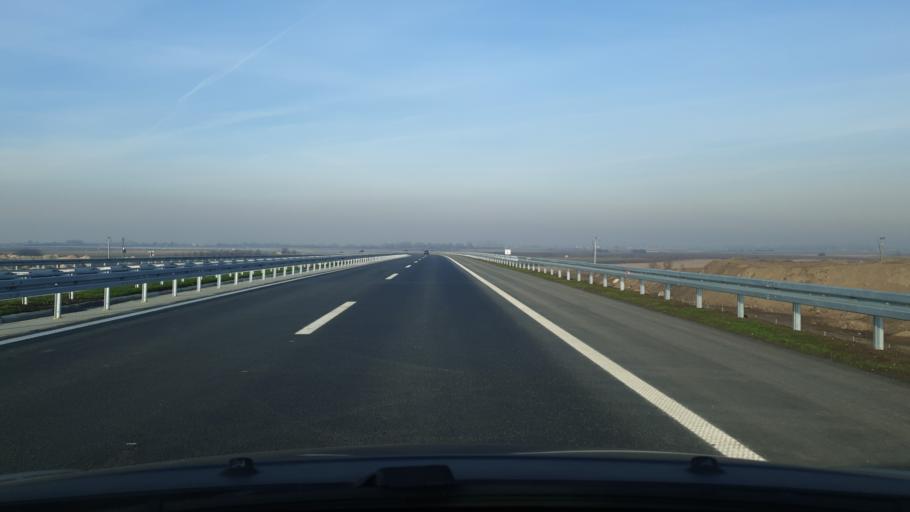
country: RS
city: Boljevci
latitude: 44.7179
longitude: 20.2585
